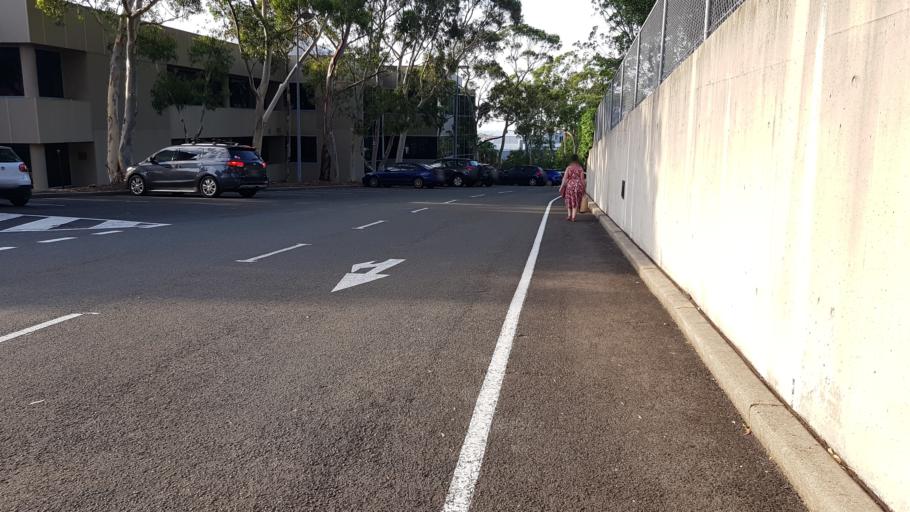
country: AU
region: New South Wales
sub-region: Warringah
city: Allambie Heights
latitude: -33.7530
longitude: 151.2485
